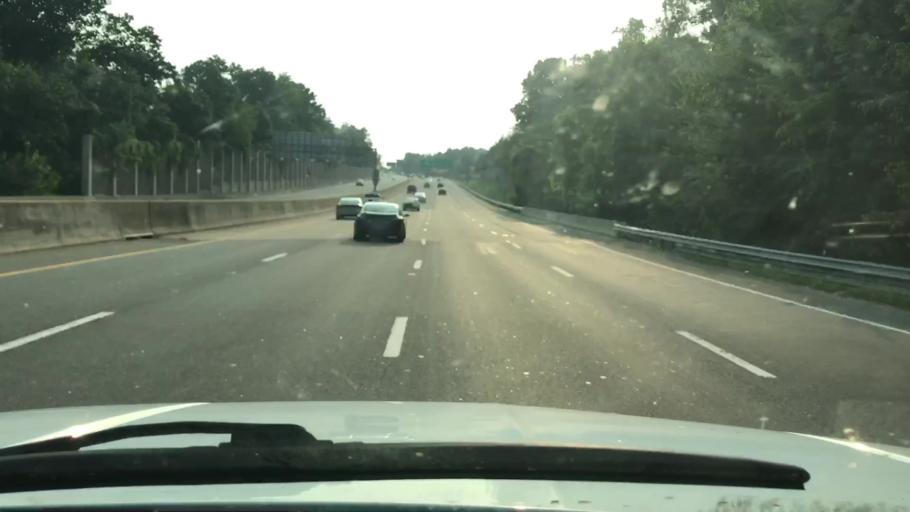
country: US
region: Virginia
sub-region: Chesterfield County
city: Bensley
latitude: 37.4435
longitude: -77.4423
